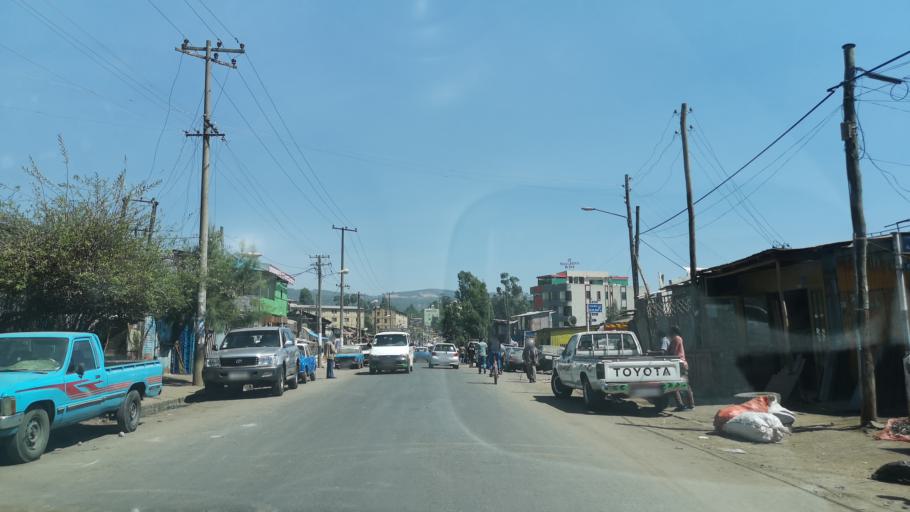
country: ET
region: Adis Abeba
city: Addis Ababa
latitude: 9.0499
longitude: 38.7478
